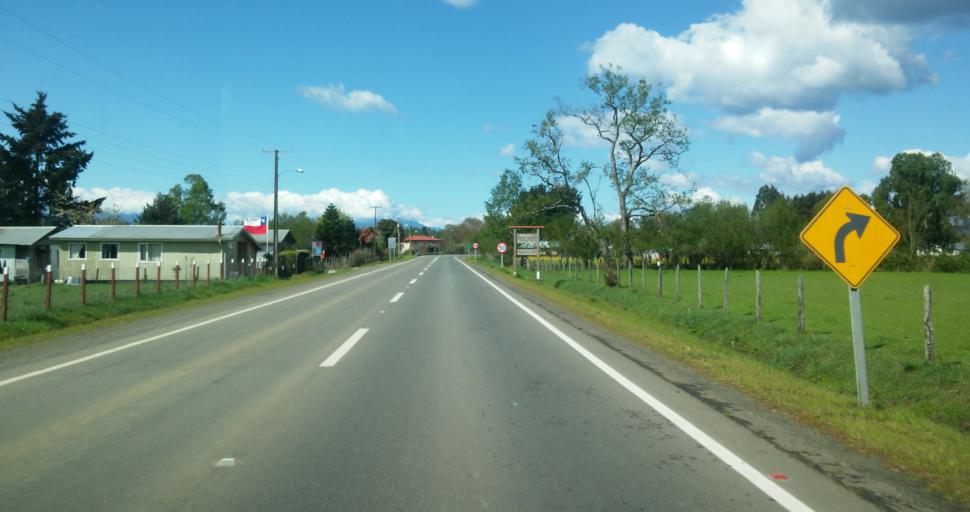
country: CL
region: Los Rios
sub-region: Provincia del Ranco
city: Rio Bueno
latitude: -40.2393
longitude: -72.5957
